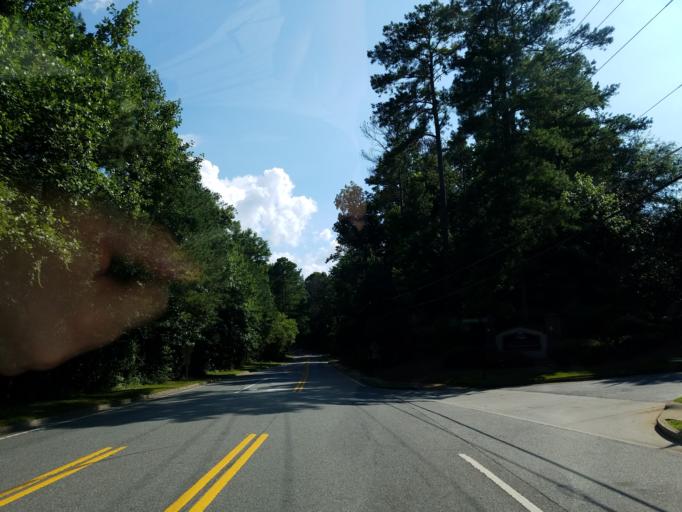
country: US
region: Georgia
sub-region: Fulton County
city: Roswell
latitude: 34.0000
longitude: -84.3342
